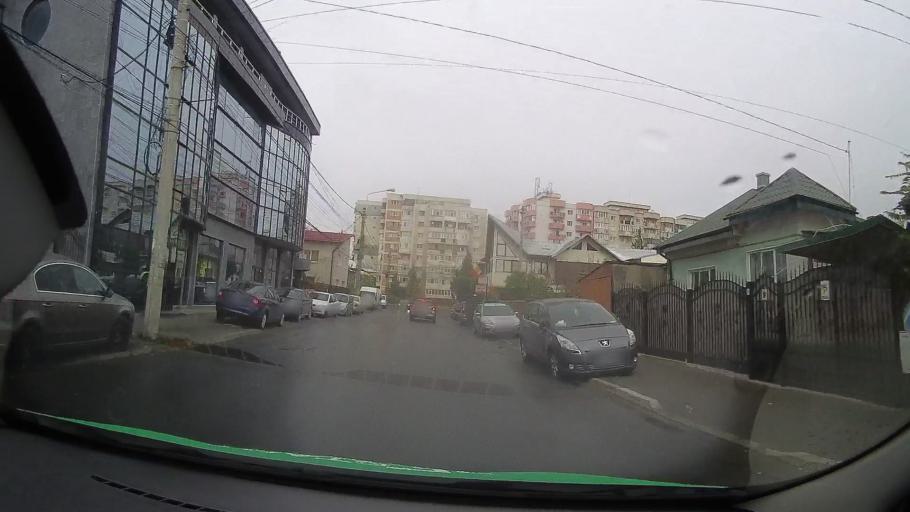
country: RO
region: Prahova
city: Ploiesti
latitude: 44.9369
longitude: 26.0045
